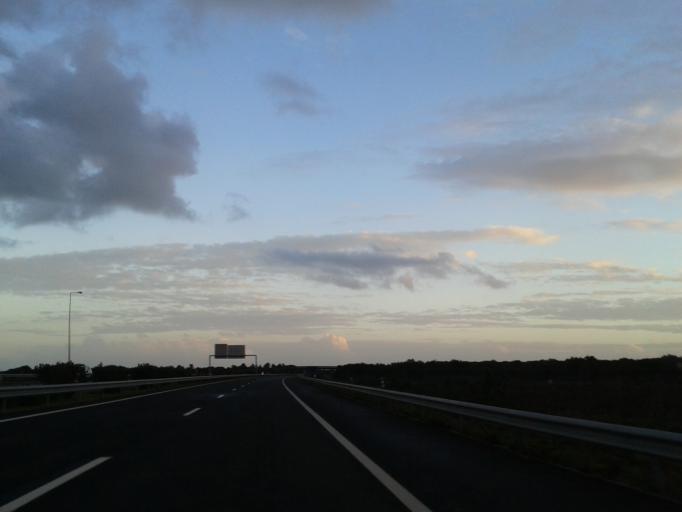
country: PT
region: Santarem
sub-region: Benavente
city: Poceirao
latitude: 38.8347
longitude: -8.7234
